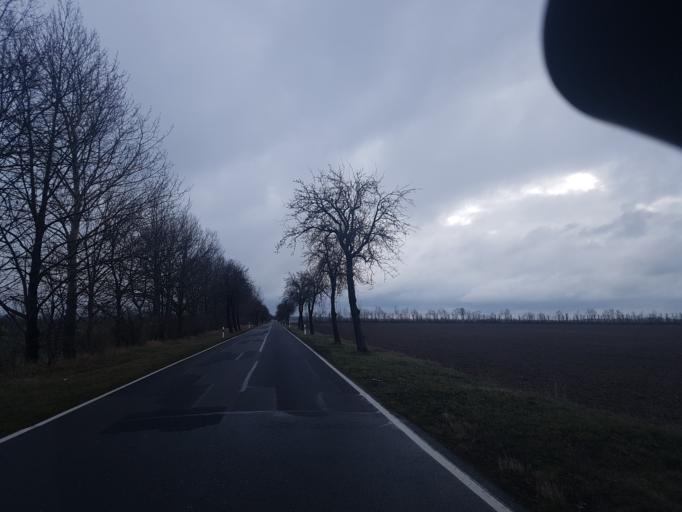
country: DE
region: Brandenburg
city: Muhlberg
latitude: 51.4182
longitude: 13.2330
